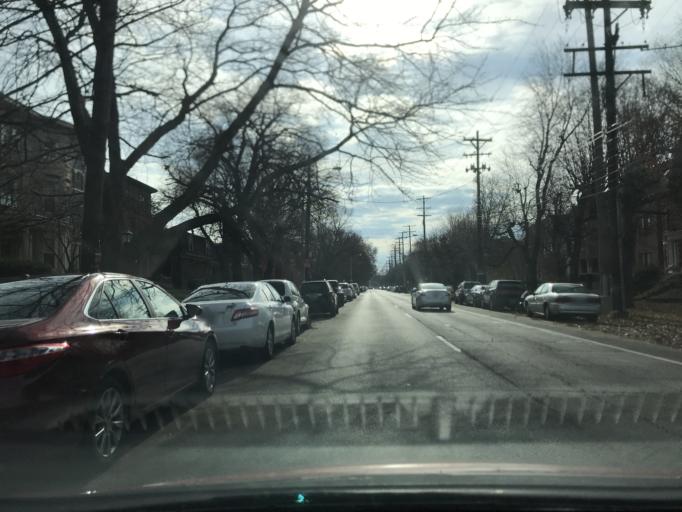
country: US
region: Kentucky
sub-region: Jefferson County
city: Louisville
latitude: 38.2256
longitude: -85.7603
